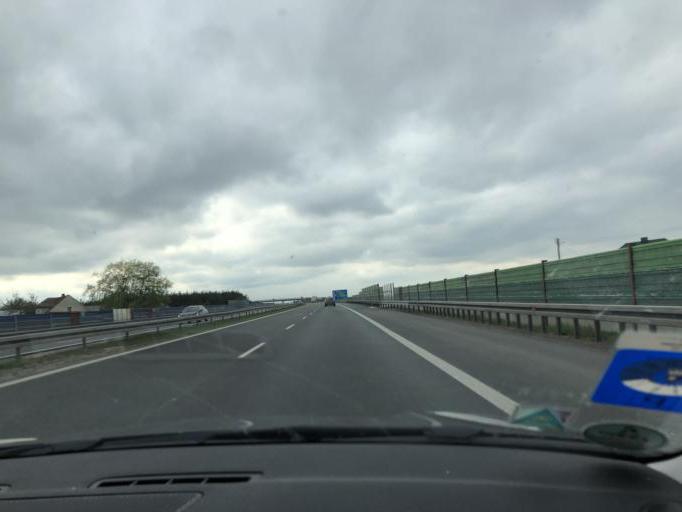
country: PL
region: Opole Voivodeship
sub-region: Powiat krapkowicki
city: Krapkowice
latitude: 50.5211
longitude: 17.9441
